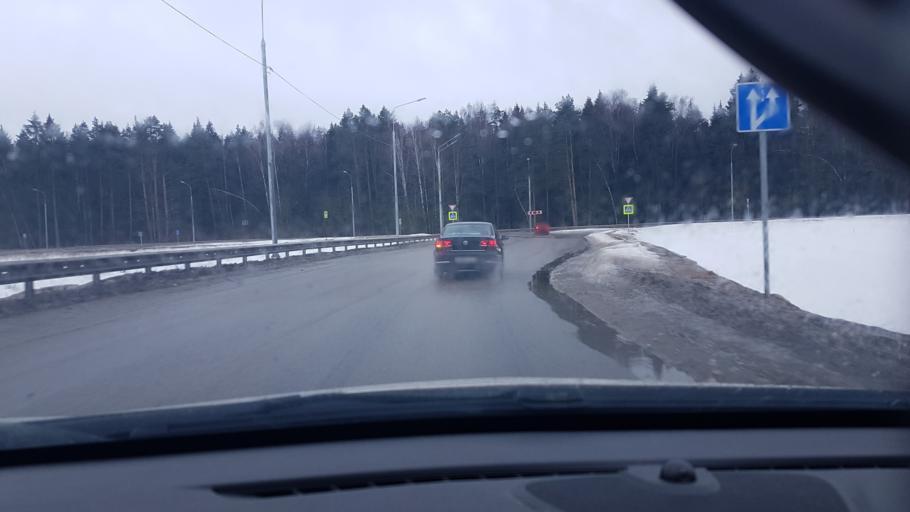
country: RU
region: Moskovskaya
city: Istra
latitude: 55.8561
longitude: 36.9358
